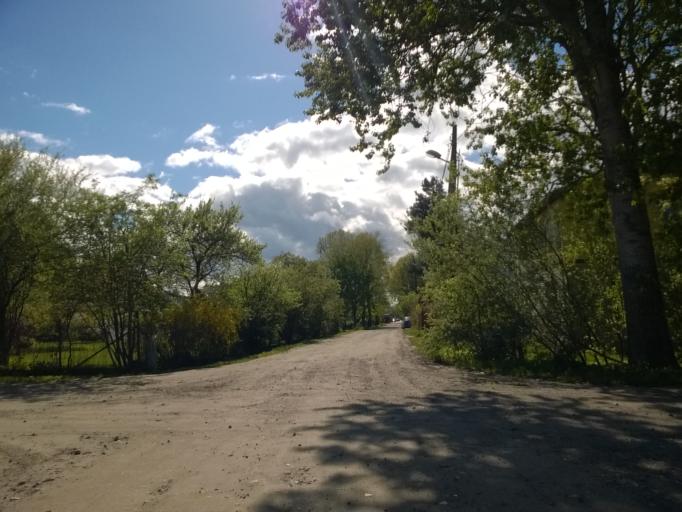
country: LV
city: Tireli
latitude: 56.9525
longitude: 23.6218
